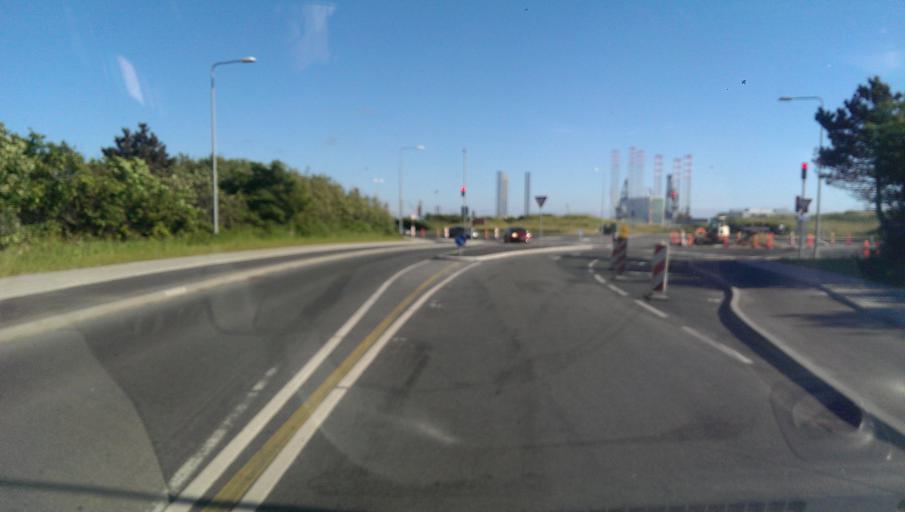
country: DK
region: South Denmark
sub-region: Esbjerg Kommune
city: Esbjerg
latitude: 55.4880
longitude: 8.4129
